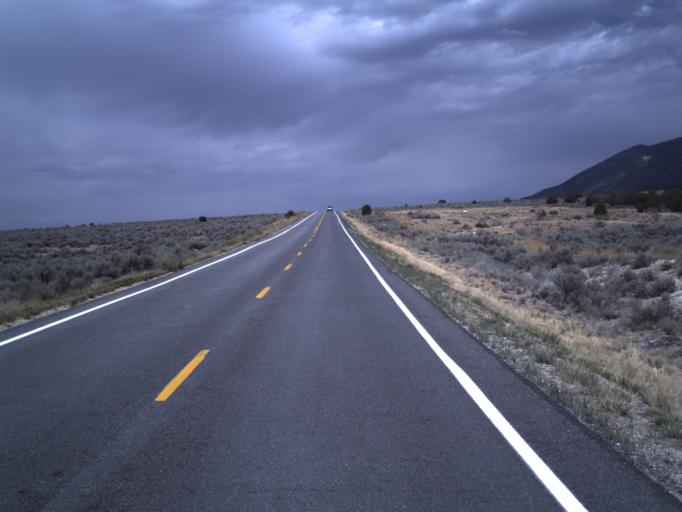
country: US
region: Utah
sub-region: Tooele County
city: Tooele
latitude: 40.3093
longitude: -112.2807
